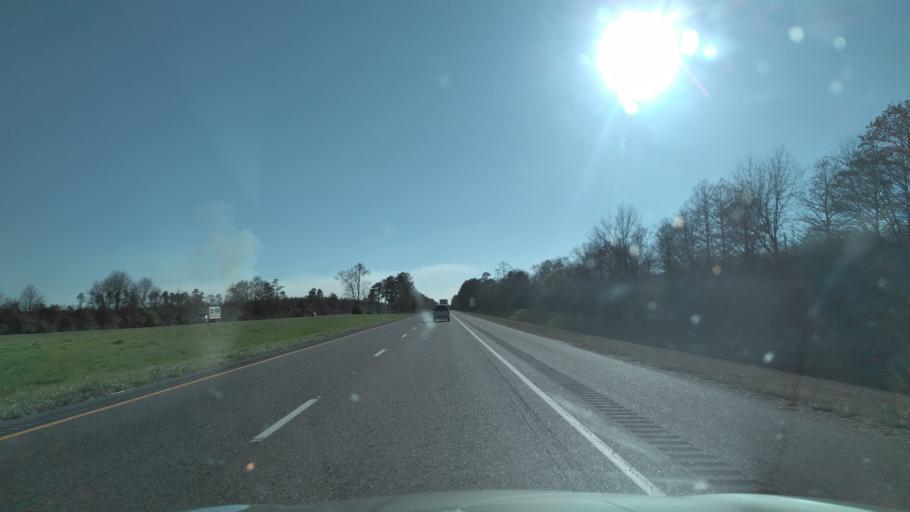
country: US
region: Alabama
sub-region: Escambia County
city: Atmore
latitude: 31.0775
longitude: -87.5442
